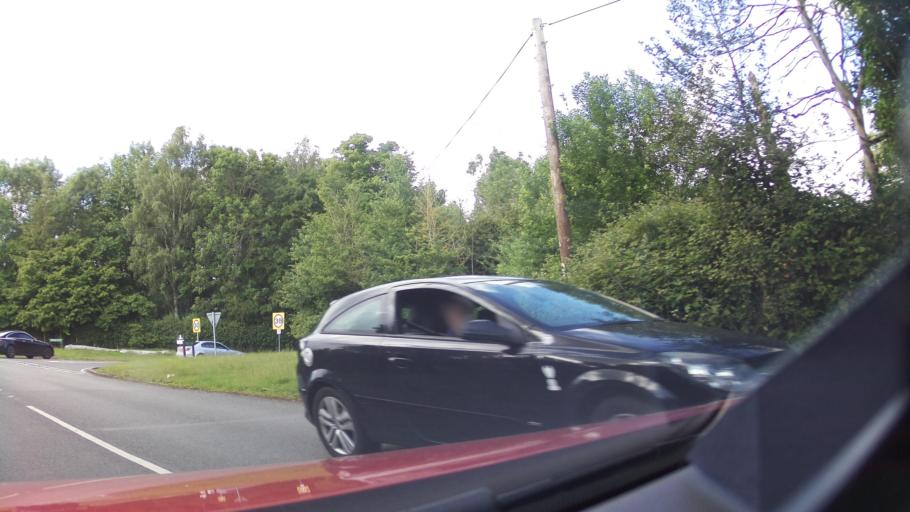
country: GB
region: England
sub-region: Hertfordshire
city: Chorleywood
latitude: 51.6664
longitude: -0.4664
